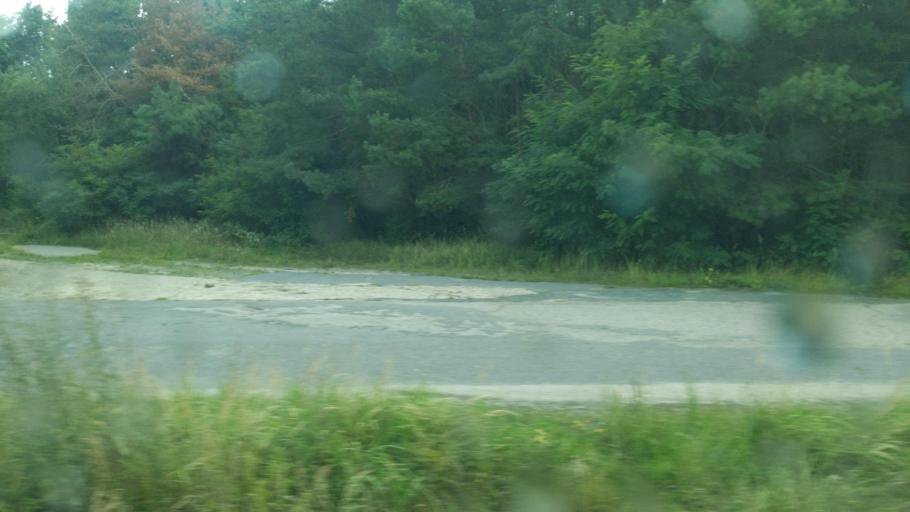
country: CZ
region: Central Bohemia
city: Poricany
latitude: 50.1199
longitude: 14.9490
